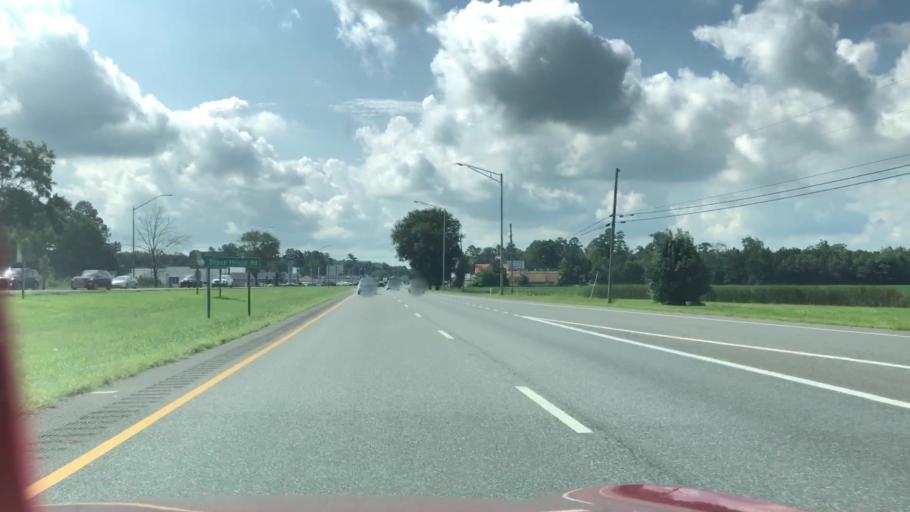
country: US
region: Maryland
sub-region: Worcester County
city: Pocomoke City
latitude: 38.0565
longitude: -75.5443
